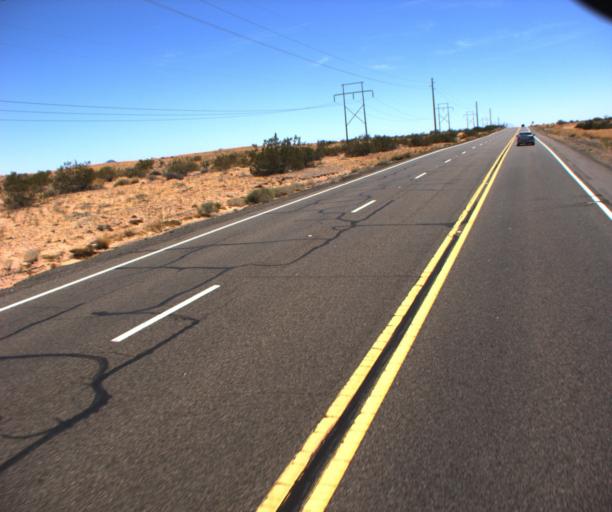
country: US
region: Arizona
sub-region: La Paz County
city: Parker
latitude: 33.9612
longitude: -114.2169
